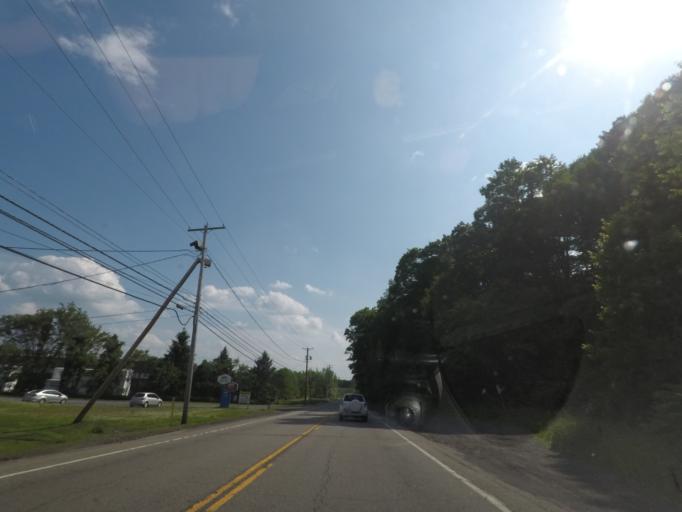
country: US
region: New York
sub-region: Ulster County
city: Marlboro
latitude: 41.5936
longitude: -73.9782
